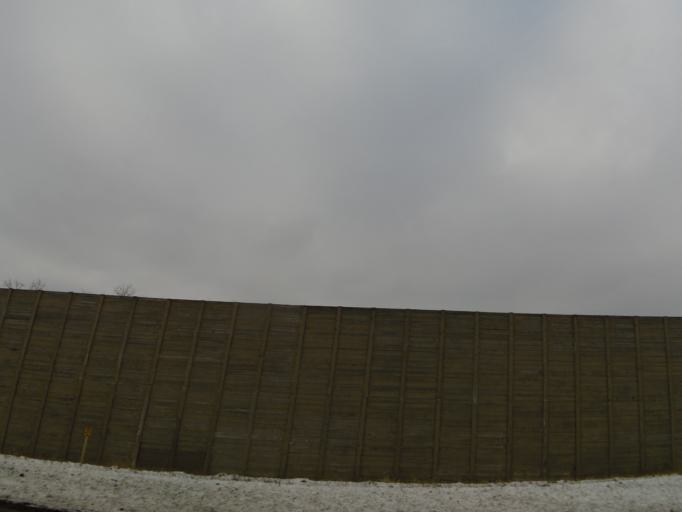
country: US
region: Minnesota
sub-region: Hennepin County
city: Hopkins
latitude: 44.9389
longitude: -93.4570
